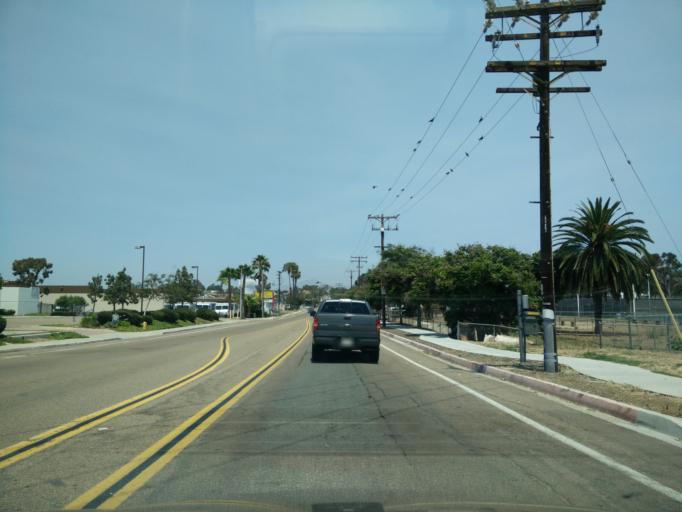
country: US
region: California
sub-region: San Diego County
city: Chula Vista
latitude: 32.6495
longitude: -117.0917
